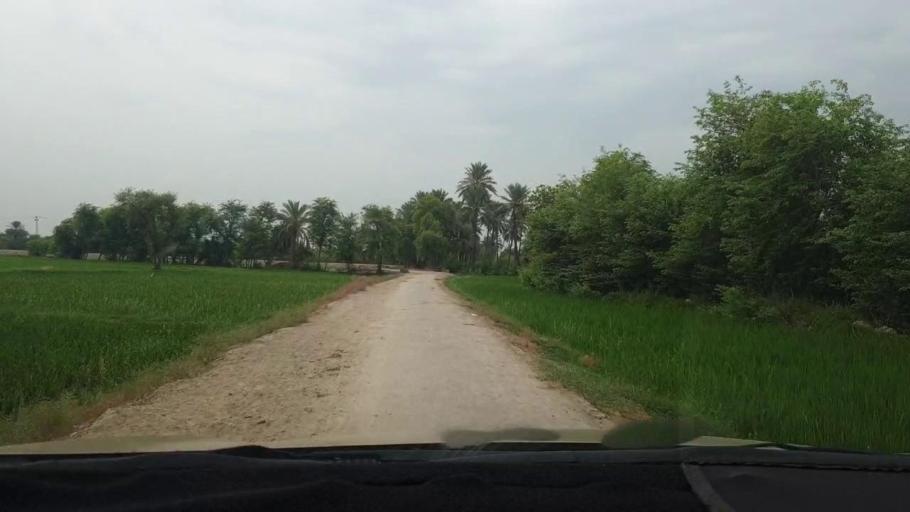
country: PK
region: Sindh
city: Larkana
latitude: 27.5732
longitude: 68.2442
